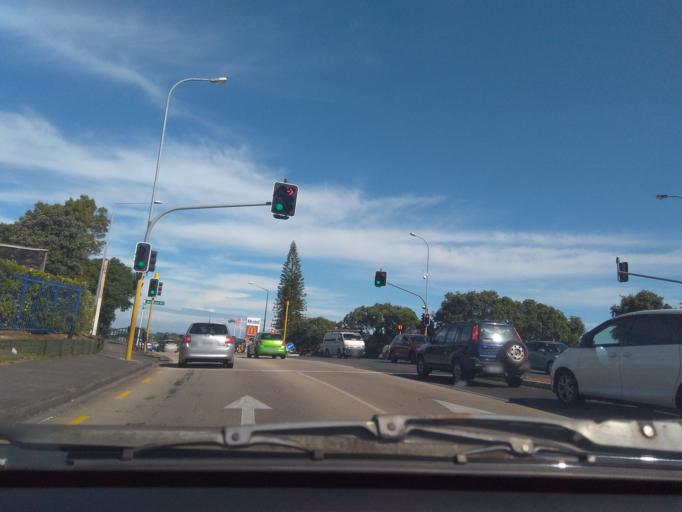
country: NZ
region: Auckland
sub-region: Auckland
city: Waitakere
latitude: -36.9080
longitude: 174.6637
